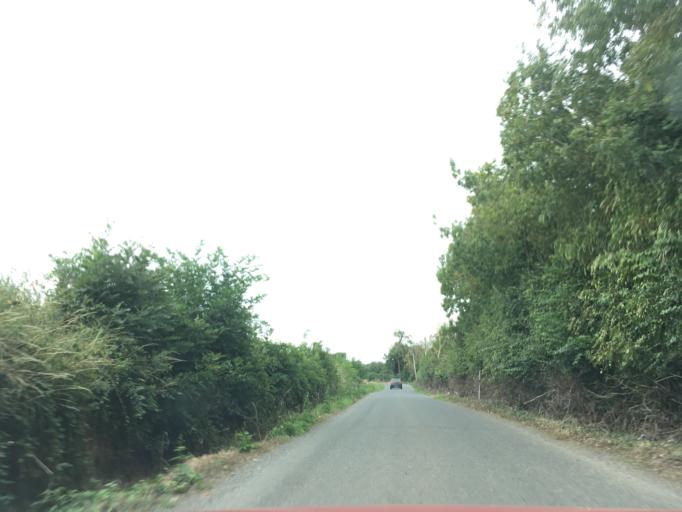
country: IE
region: Munster
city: Cahir
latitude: 52.4618
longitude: -8.0065
